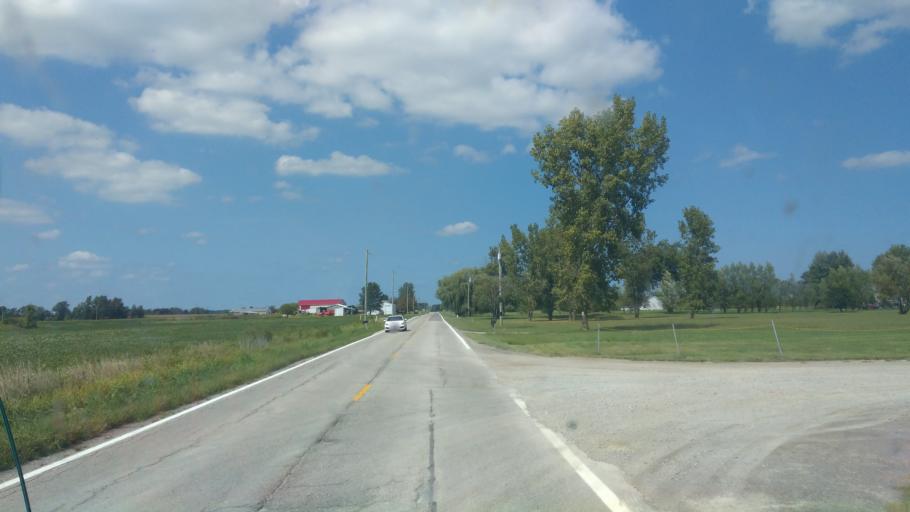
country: US
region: Ohio
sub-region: Union County
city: Richwood
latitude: 40.3948
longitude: -83.4535
